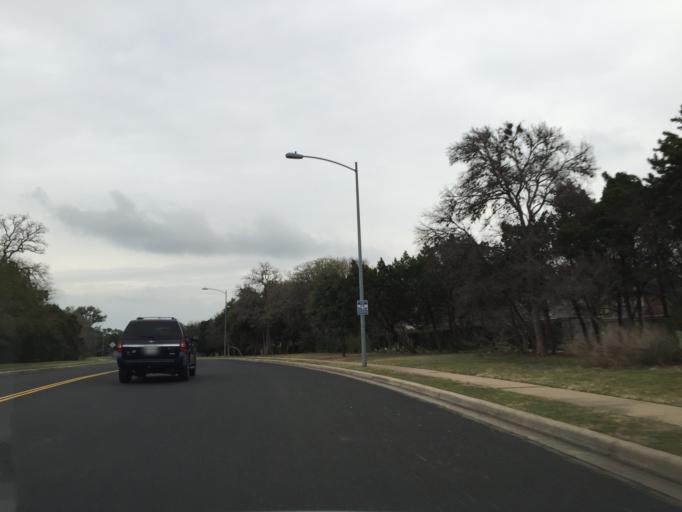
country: US
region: Texas
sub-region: Travis County
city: Rollingwood
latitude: 30.2421
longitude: -97.8308
